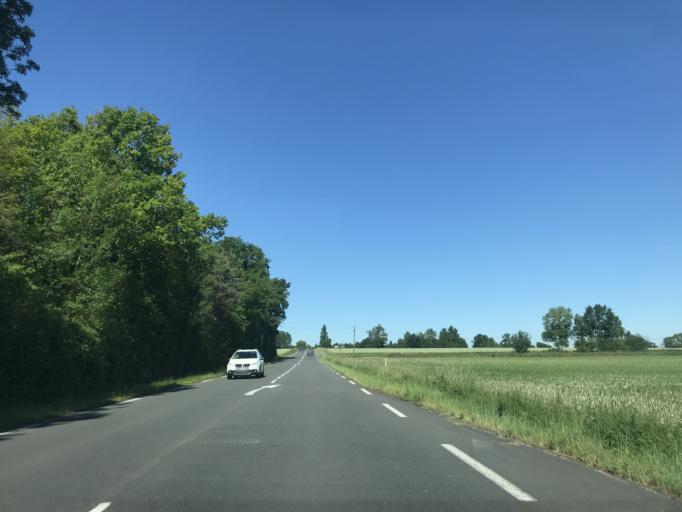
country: FR
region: Poitou-Charentes
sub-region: Departement de la Charente
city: Barbezieux-Saint-Hilaire
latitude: 45.4974
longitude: -0.2382
